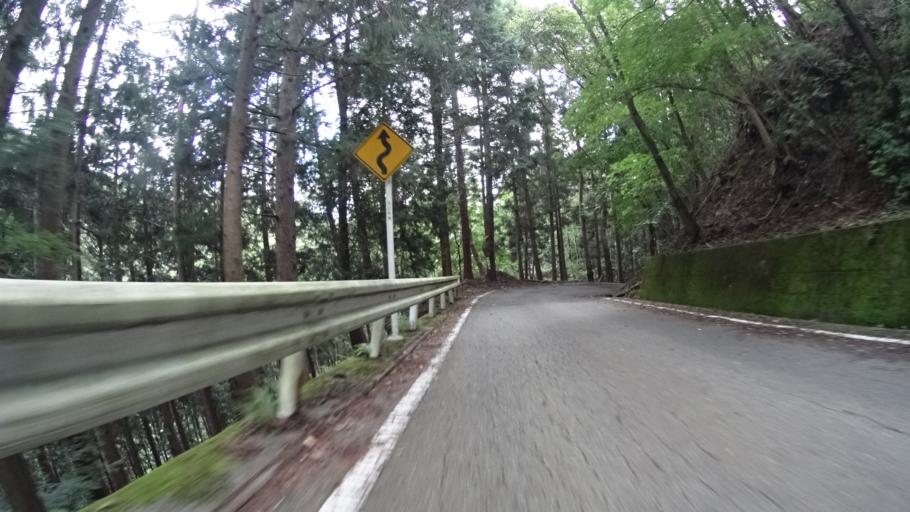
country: JP
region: Yamanashi
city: Enzan
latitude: 35.6040
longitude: 138.7974
